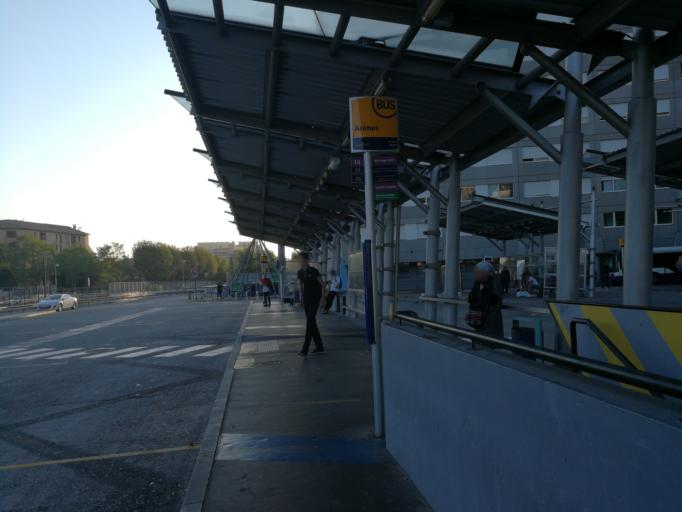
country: FR
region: Midi-Pyrenees
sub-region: Departement de la Haute-Garonne
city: Toulouse
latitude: 43.5937
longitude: 1.4183
